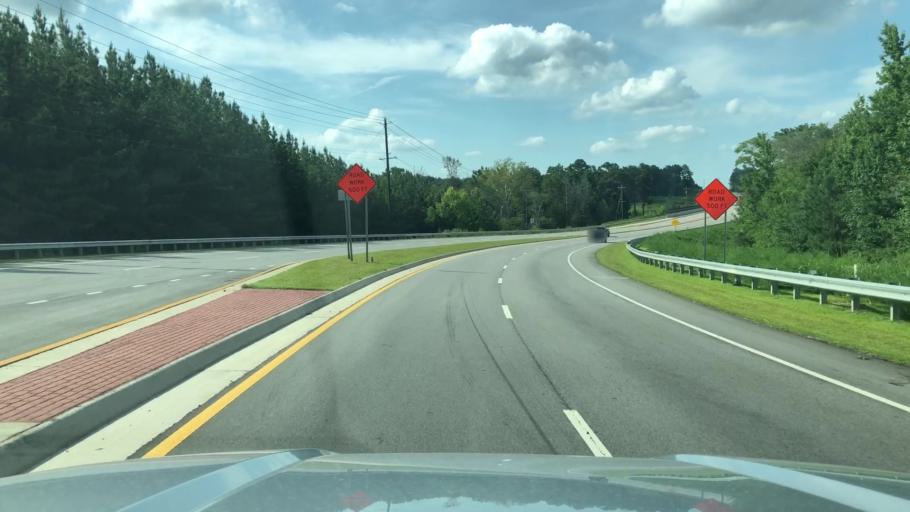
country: US
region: Georgia
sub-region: Paulding County
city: Hiram
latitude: 33.8787
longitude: -84.7816
